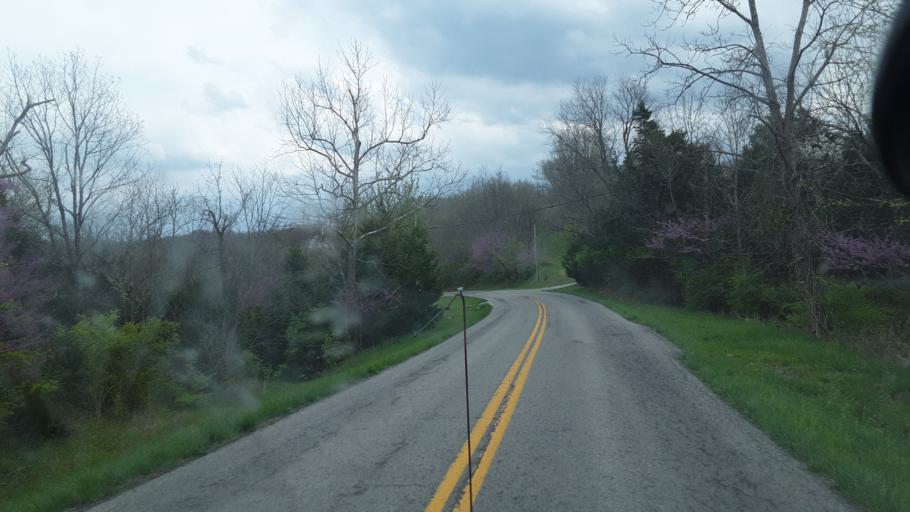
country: US
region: Kentucky
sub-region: Grant County
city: Dry Ridge
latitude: 38.6427
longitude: -84.7232
